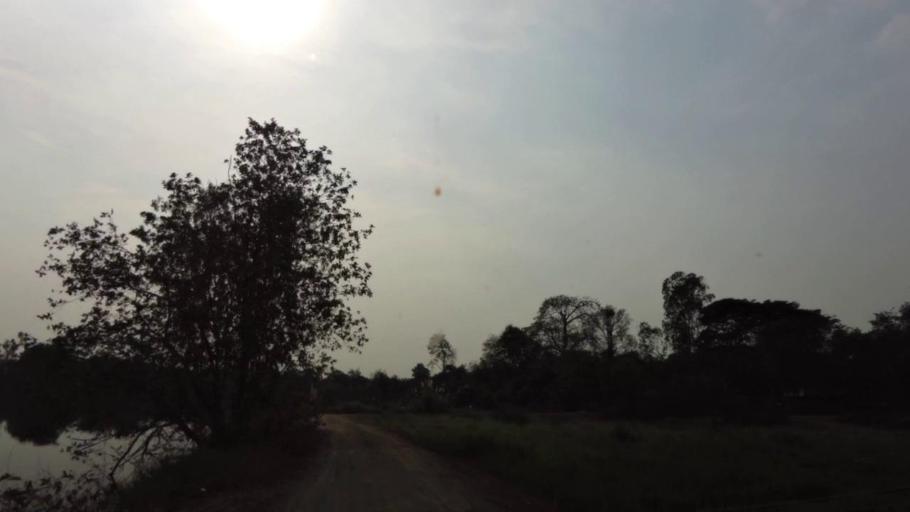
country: TH
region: Phra Nakhon Si Ayutthaya
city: Phra Nakhon Si Ayutthaya
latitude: 14.3414
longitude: 100.5683
